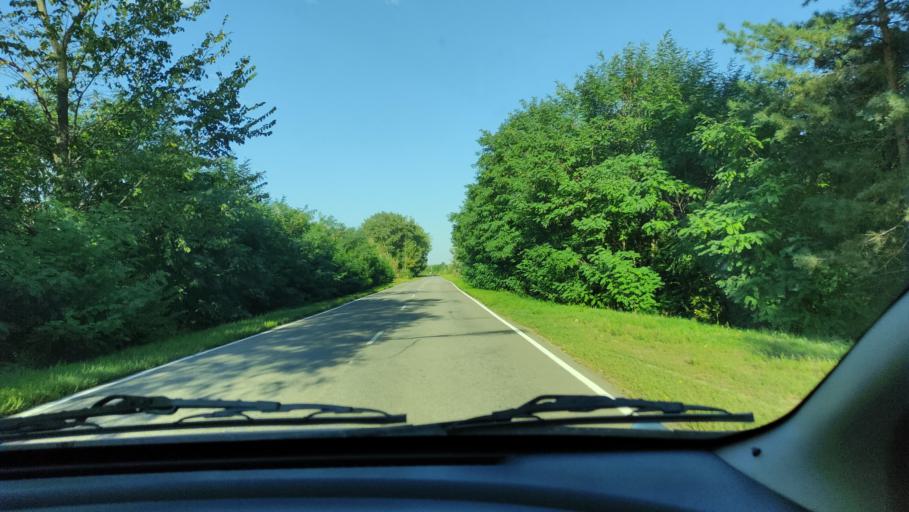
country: RU
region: Voronezj
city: Verkhniy Mamon
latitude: 50.1177
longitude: 40.2932
